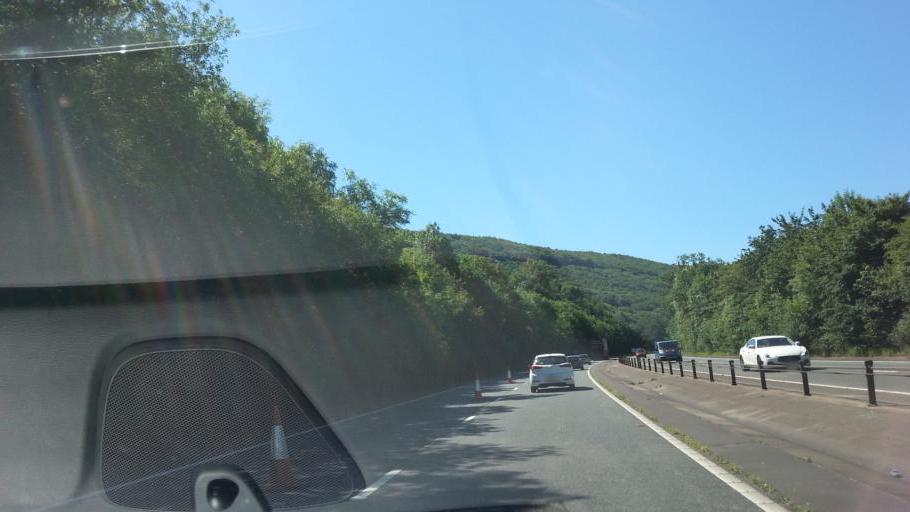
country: GB
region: Wales
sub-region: Monmouthshire
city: Llangybi
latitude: 51.6467
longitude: -2.8804
